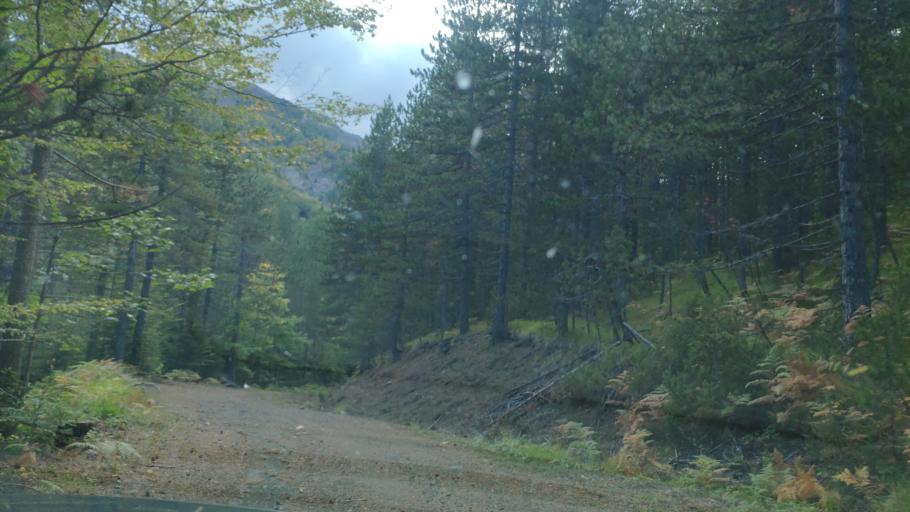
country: AL
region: Korce
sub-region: Rrethi i Devollit
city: Miras
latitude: 40.3415
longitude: 20.8991
